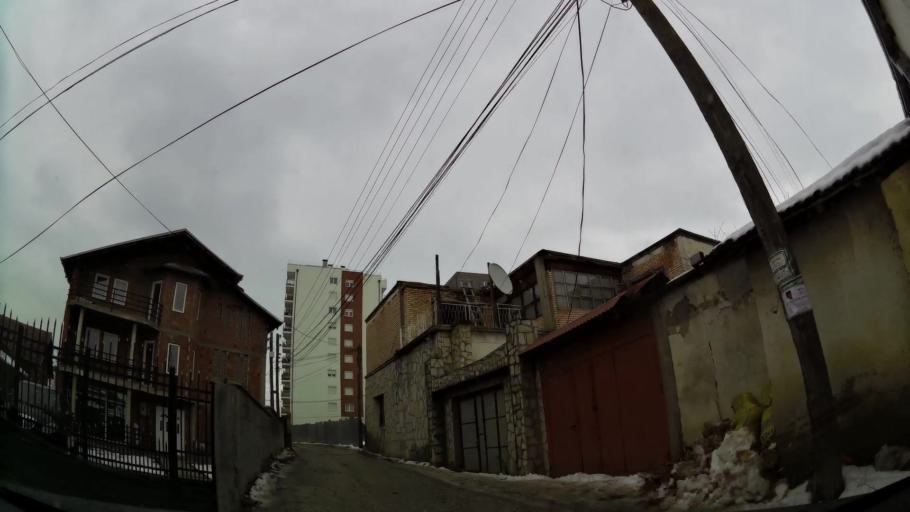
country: XK
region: Pristina
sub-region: Komuna e Prishtines
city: Pristina
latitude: 42.6603
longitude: 21.1735
